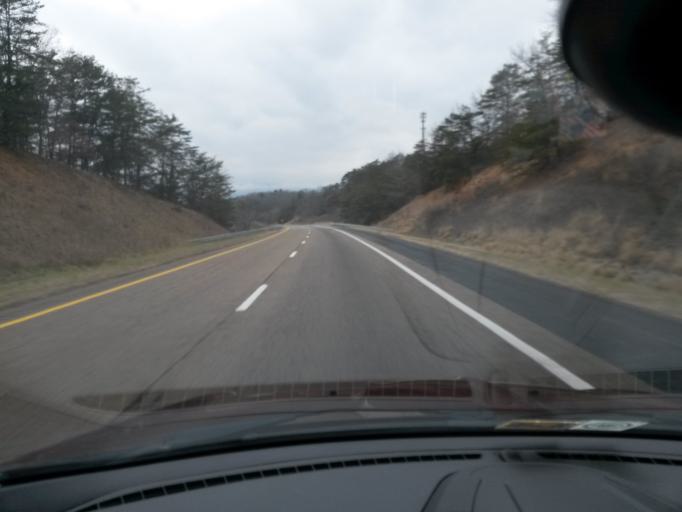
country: US
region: Virginia
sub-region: Alleghany County
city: Clifton Forge
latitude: 37.8317
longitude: -79.7599
